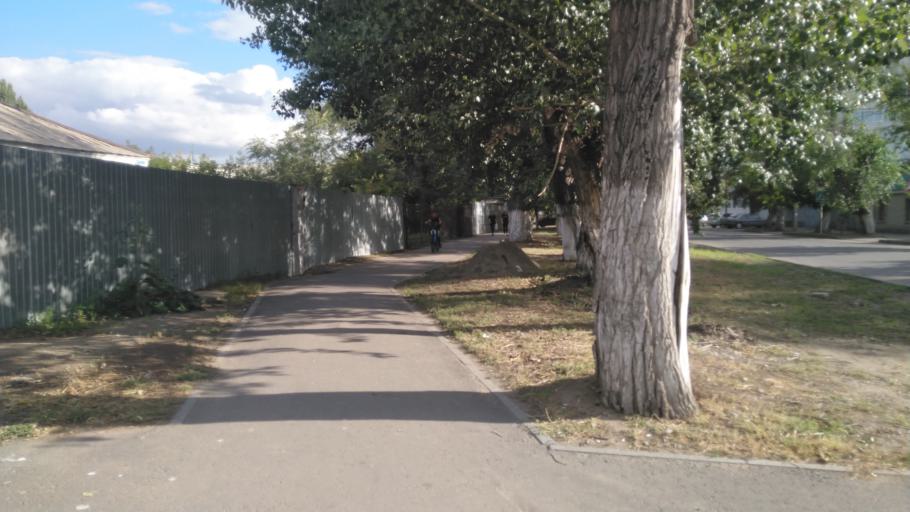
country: KZ
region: Pavlodar
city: Pavlodar
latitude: 52.2768
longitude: 76.9465
